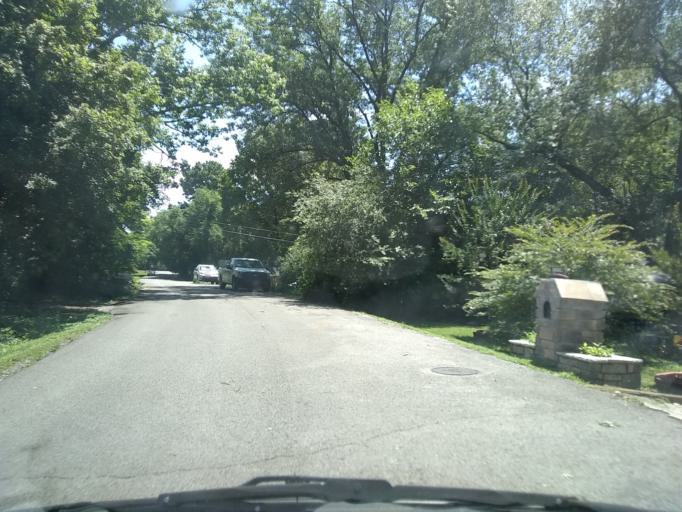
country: US
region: Tennessee
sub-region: Davidson County
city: Nashville
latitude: 36.1292
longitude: -86.7050
